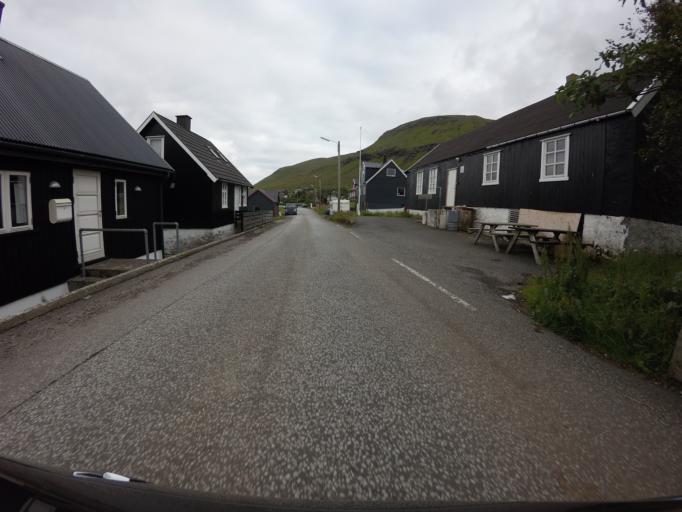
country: FO
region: Eysturoy
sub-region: Eidi
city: Eidi
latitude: 62.1869
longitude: -7.0357
